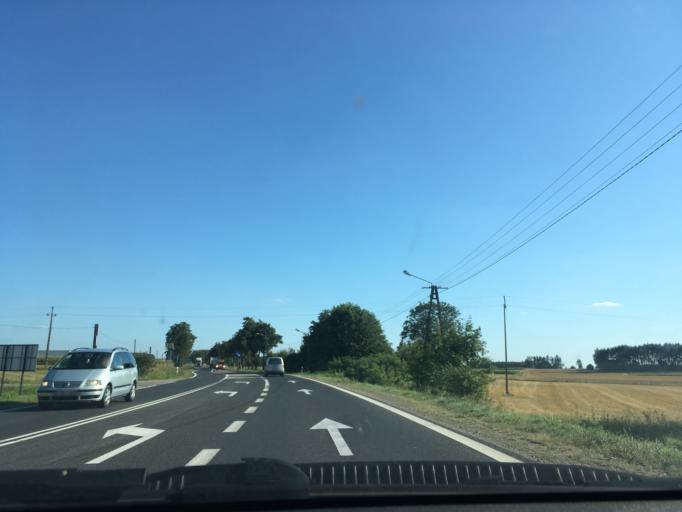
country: PL
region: Podlasie
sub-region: Powiat sokolski
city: Janow
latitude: 53.4402
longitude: 23.0955
